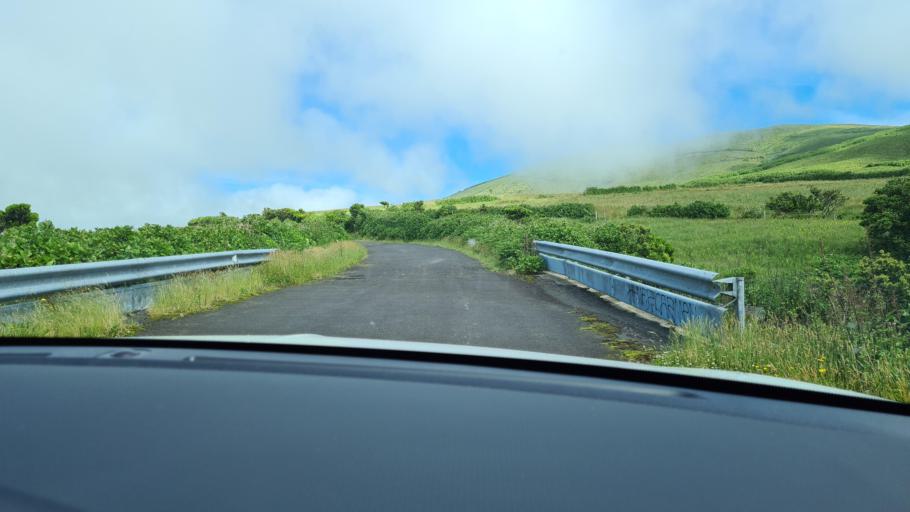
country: PT
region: Azores
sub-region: Sao Roque do Pico
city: Sao Roque do Pico
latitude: 38.6700
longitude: -28.1318
